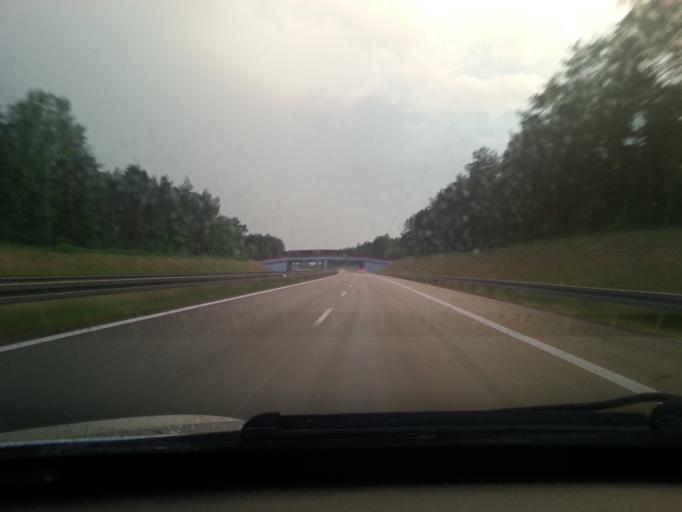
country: PL
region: Lodz Voivodeship
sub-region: Powiat pabianicki
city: Dobron
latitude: 51.6655
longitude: 19.2810
